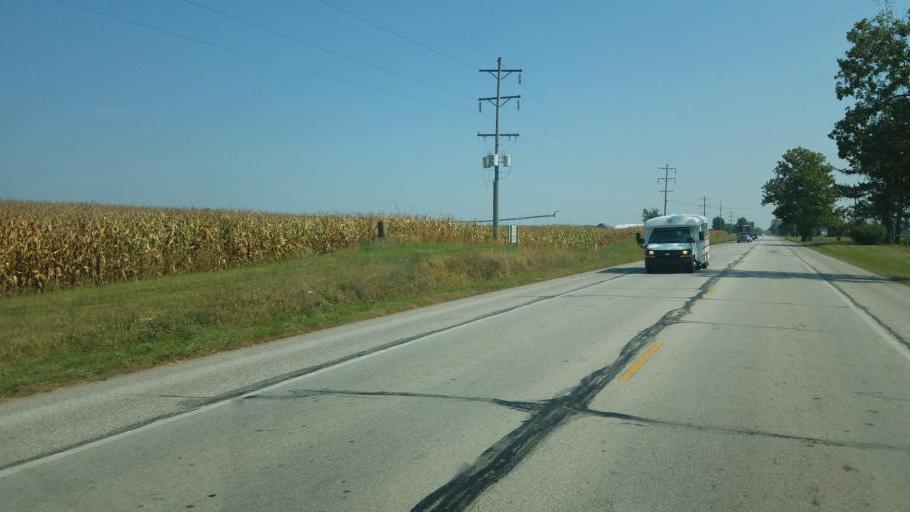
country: US
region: Indiana
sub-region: LaGrange County
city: Topeka
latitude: 41.6405
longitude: -85.5268
